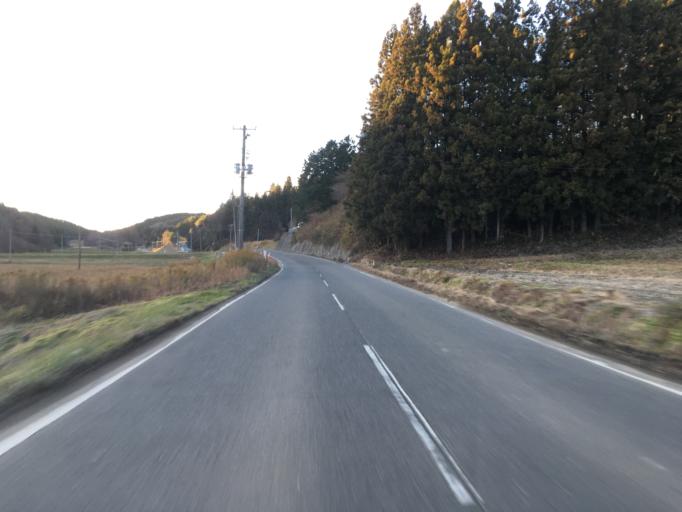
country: JP
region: Fukushima
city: Funehikimachi-funehiki
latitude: 37.2721
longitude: 140.5761
